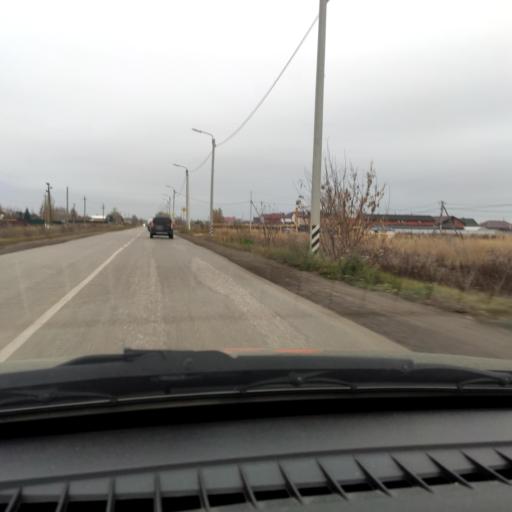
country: RU
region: Samara
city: Podstepki
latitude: 53.5224
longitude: 49.1652
